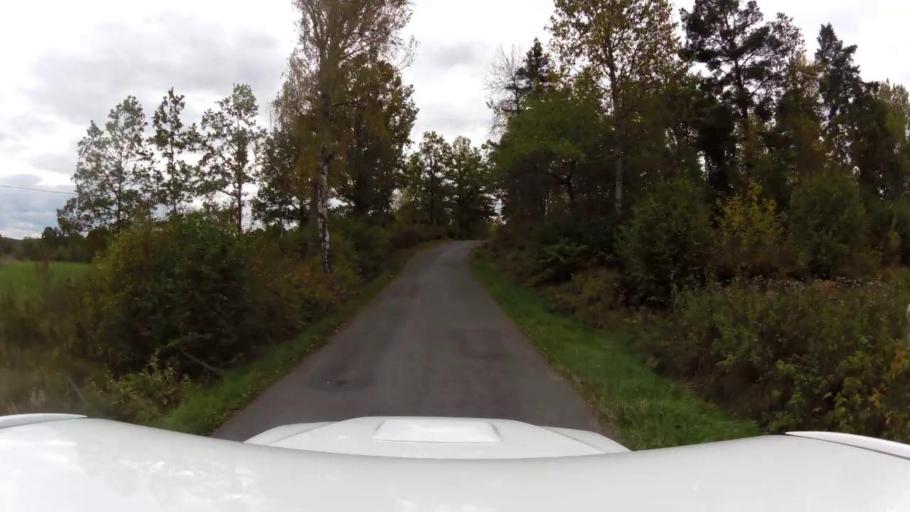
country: SE
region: OEstergoetland
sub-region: Kinda Kommun
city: Rimforsa
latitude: 58.2247
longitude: 15.6225
